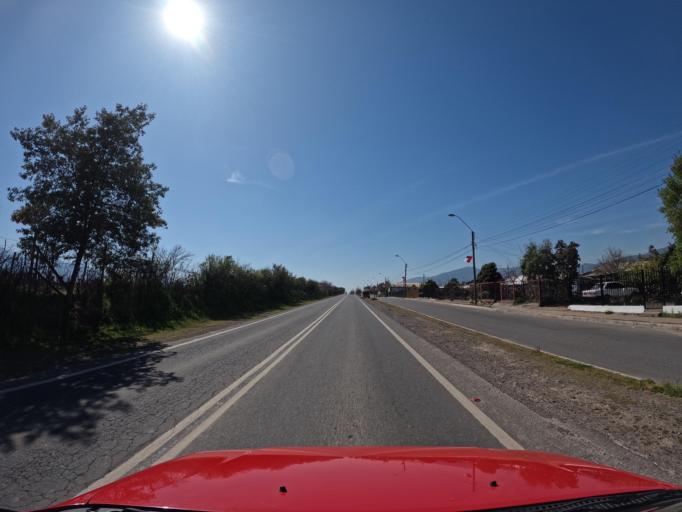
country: CL
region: Maule
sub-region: Provincia de Curico
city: Rauco
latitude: -35.0445
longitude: -71.4613
